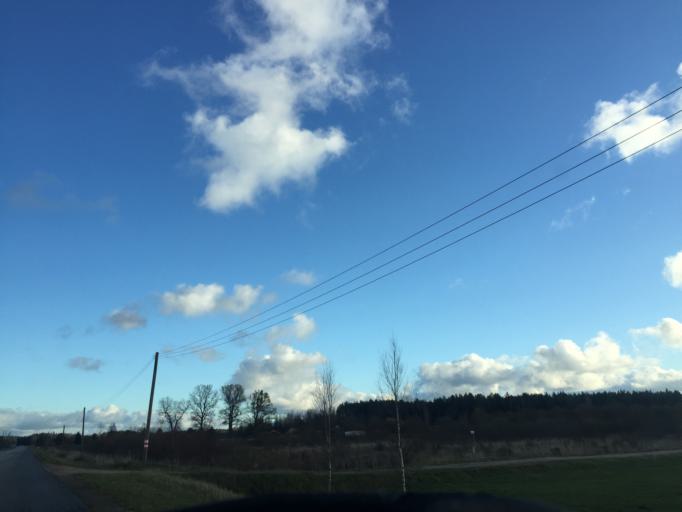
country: LV
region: Incukalns
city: Incukalns
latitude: 57.0940
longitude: 24.7076
